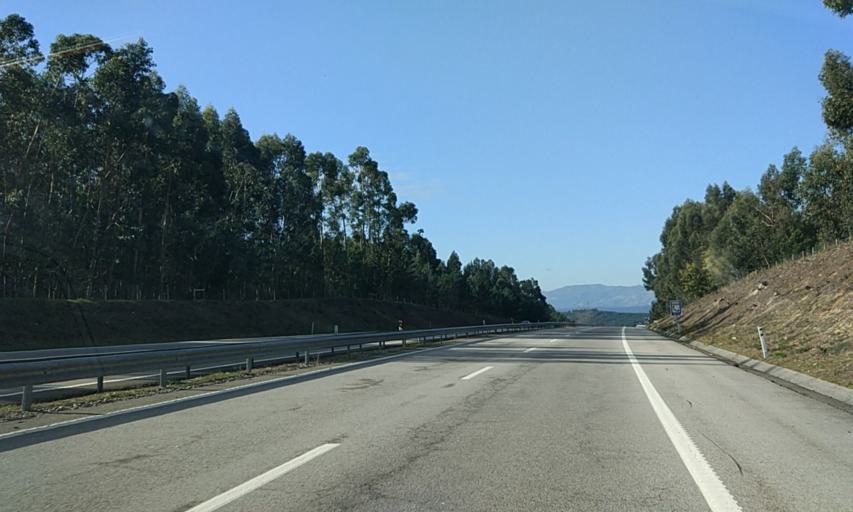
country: PT
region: Viseu
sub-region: Viseu
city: Campo
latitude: 40.7142
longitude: -7.9343
